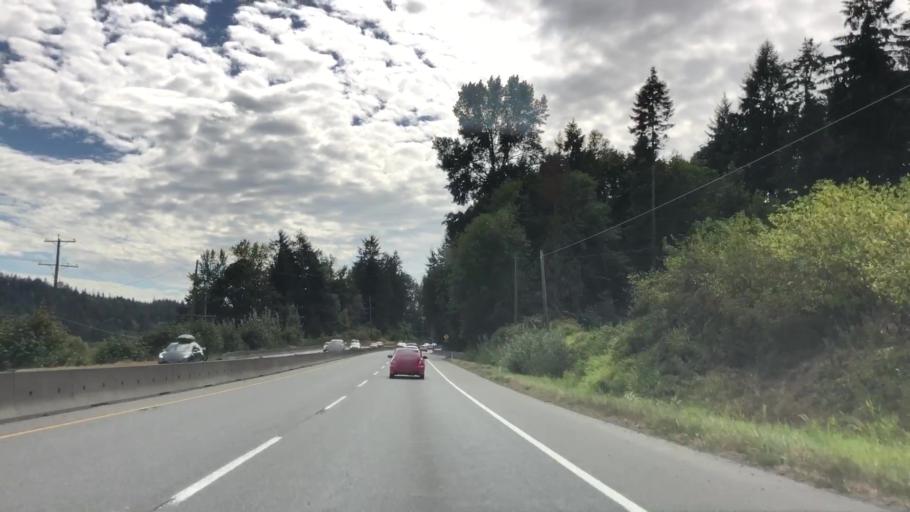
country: CA
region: British Columbia
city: North Cowichan
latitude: 48.8690
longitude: -123.7113
